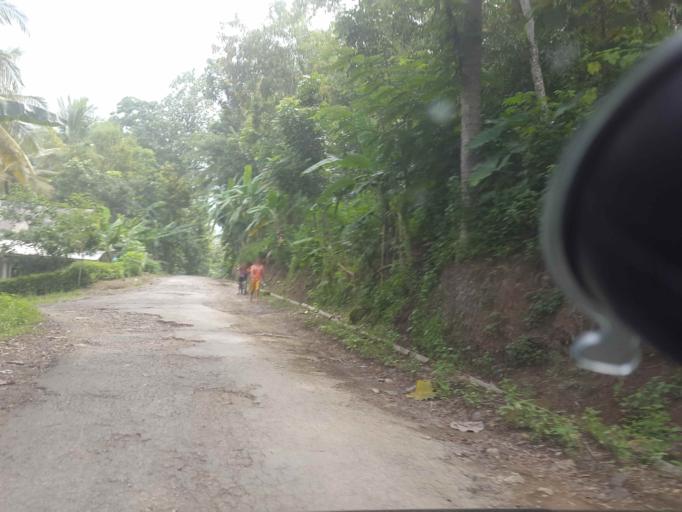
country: ID
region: Central Java
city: Kaliduren
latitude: -7.5584
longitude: 109.1021
